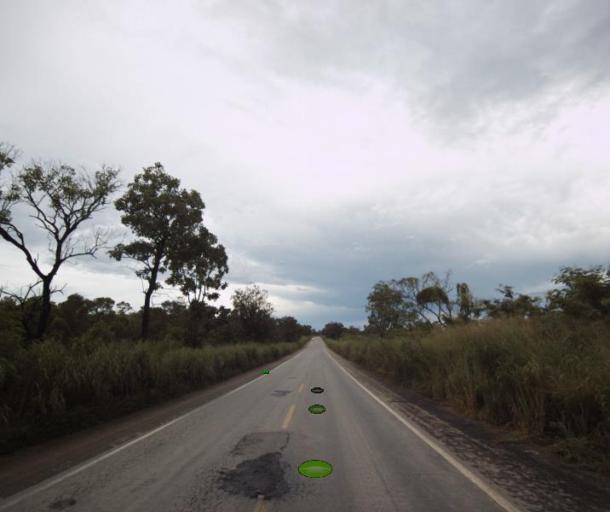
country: BR
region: Goias
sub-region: Porangatu
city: Porangatu
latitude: -13.5556
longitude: -49.0705
